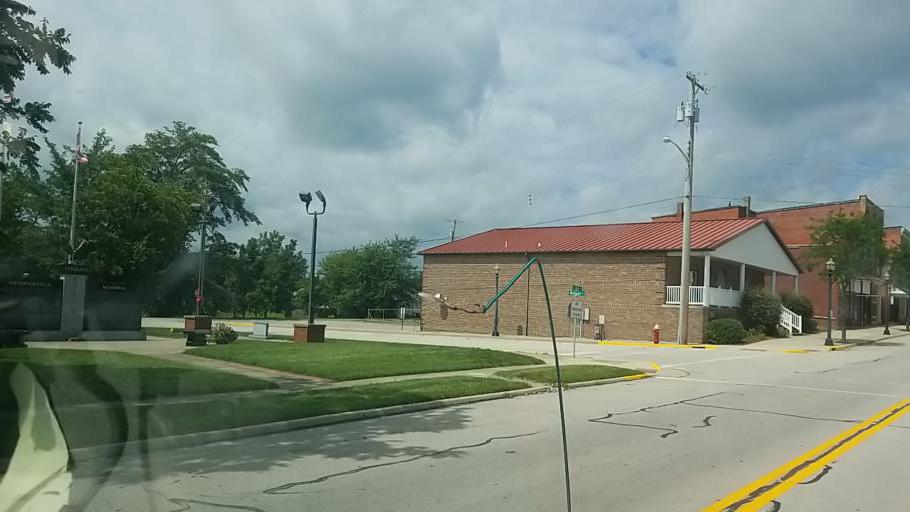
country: US
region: Ohio
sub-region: Fayette County
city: Jeffersonville
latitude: 39.6531
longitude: -83.5621
